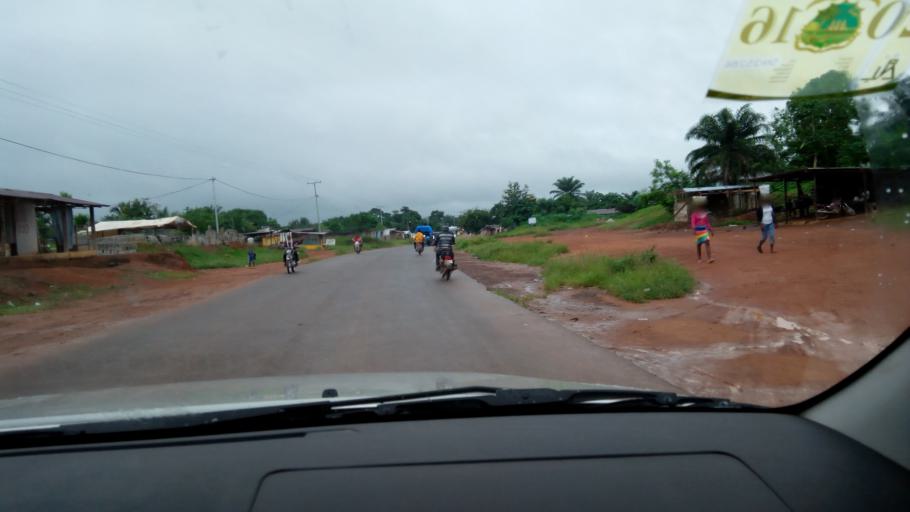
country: LR
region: Nimba
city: Sanniquellie
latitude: 7.2222
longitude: -8.9784
